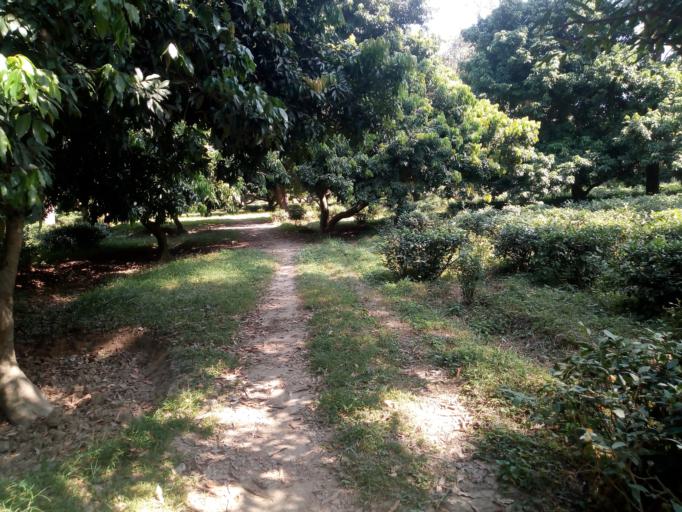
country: IN
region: Uttarakhand
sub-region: Dehradun
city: Harbatpur
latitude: 30.4456
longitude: 77.7452
